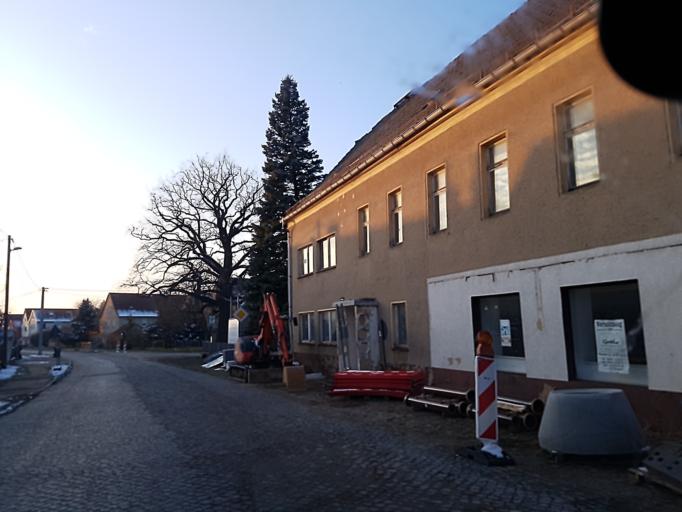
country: DE
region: Saxony
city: Strehla
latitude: 51.3873
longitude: 13.2011
